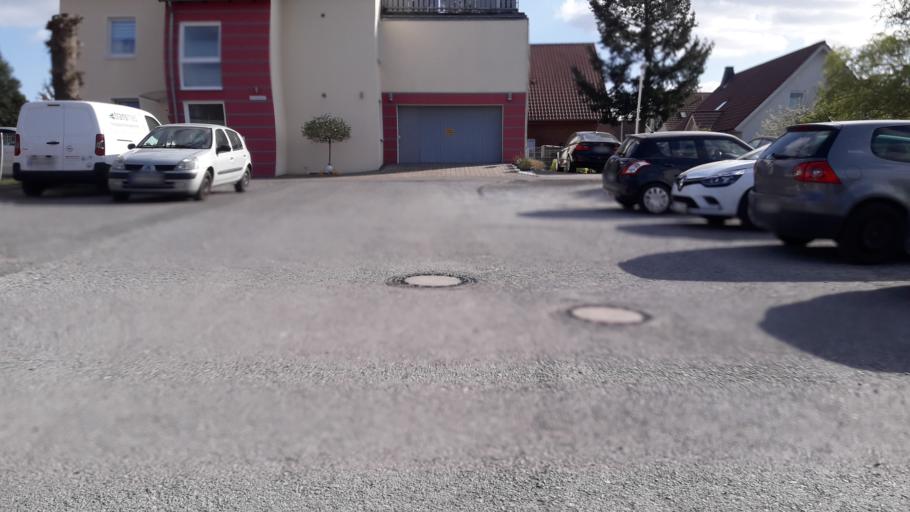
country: DE
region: North Rhine-Westphalia
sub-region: Regierungsbezirk Detmold
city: Paderborn
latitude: 51.7254
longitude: 8.7244
